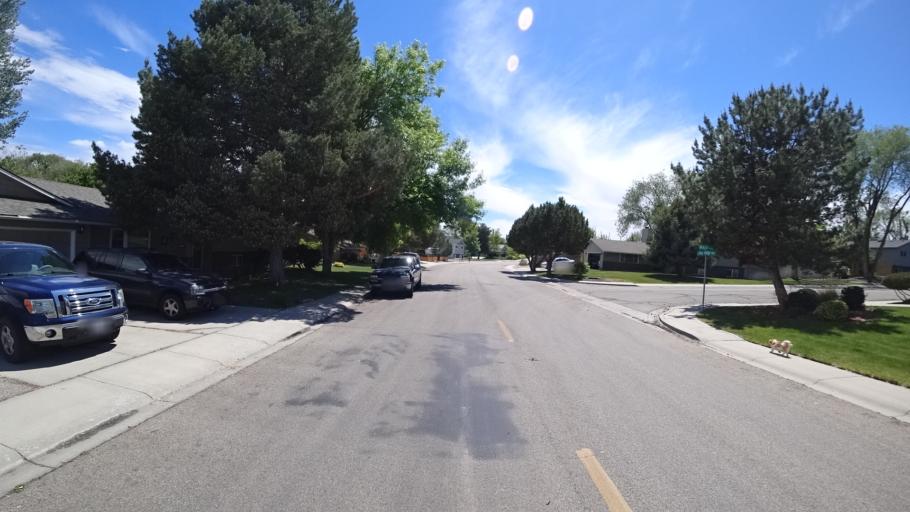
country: US
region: Idaho
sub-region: Ada County
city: Meridian
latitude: 43.5682
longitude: -116.3250
